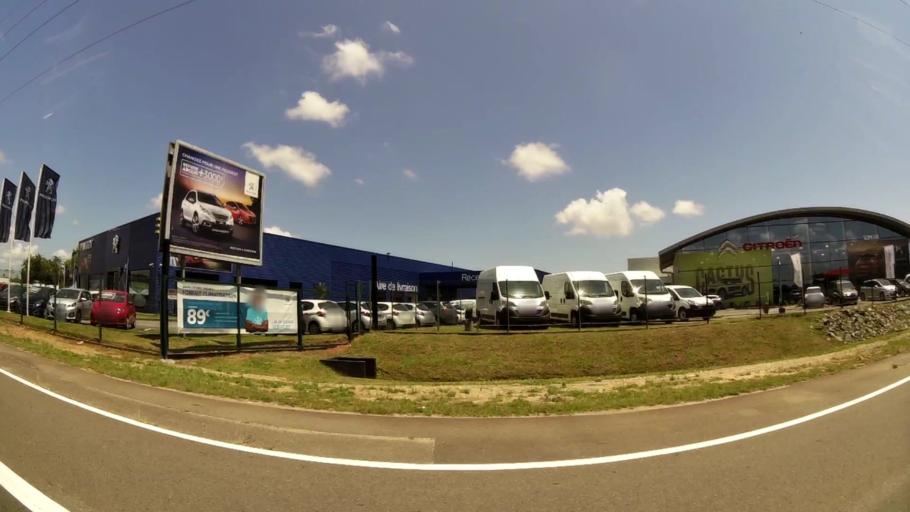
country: GF
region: Guyane
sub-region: Guyane
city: Cayenne
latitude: 4.8977
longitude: -52.3279
